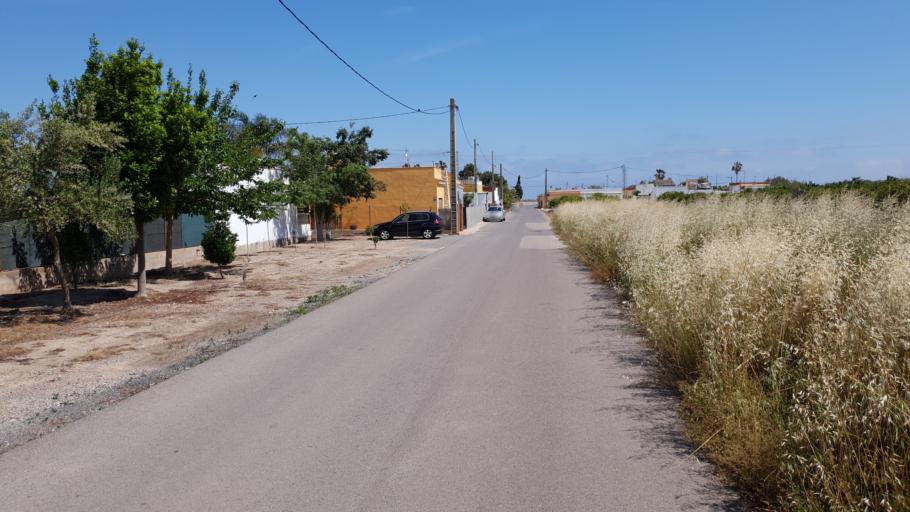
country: ES
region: Valencia
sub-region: Provincia de Castello
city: Burriana
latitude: 39.8593
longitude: -0.0879
